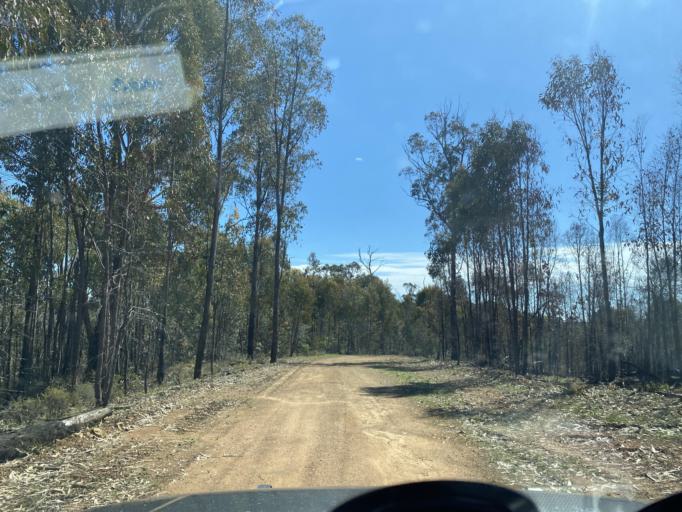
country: AU
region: Victoria
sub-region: Benalla
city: Benalla
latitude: -36.7374
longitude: 146.1815
